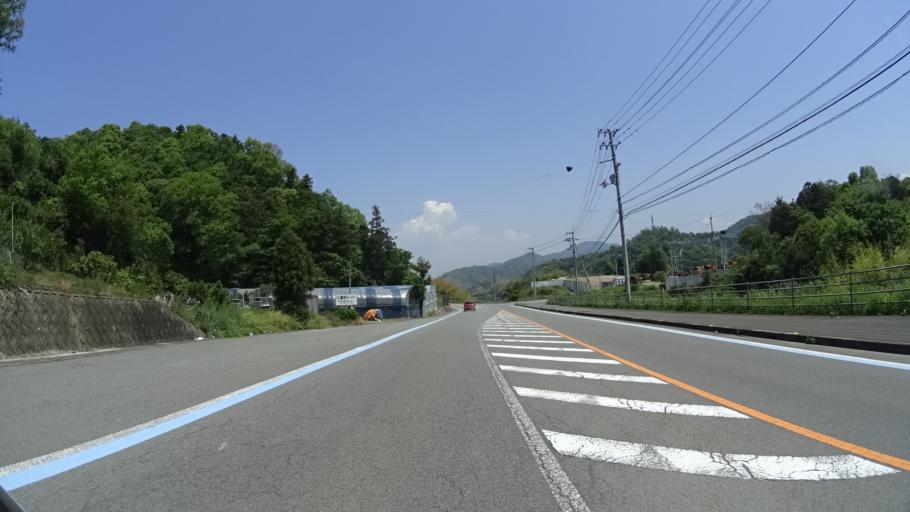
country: JP
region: Ehime
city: Iyo
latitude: 33.7220
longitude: 132.6795
